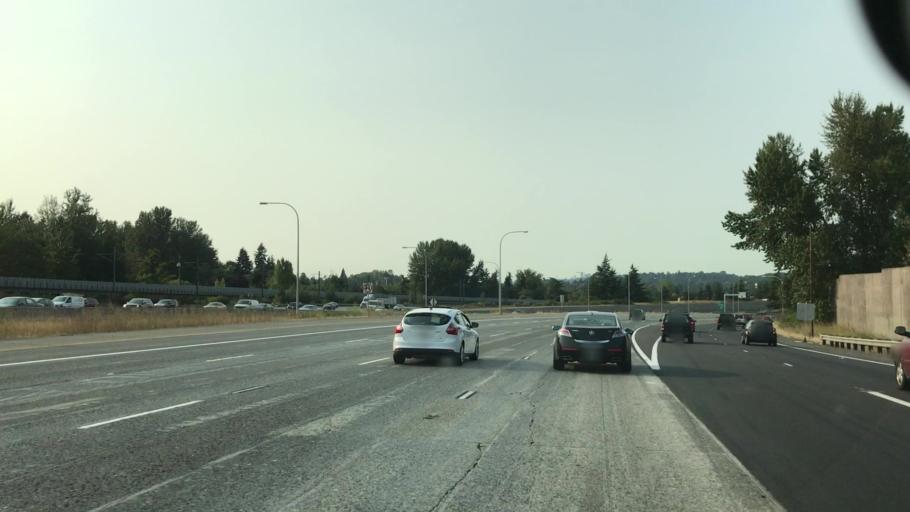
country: US
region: Washington
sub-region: King County
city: Tukwila
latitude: 47.4777
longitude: -122.2710
